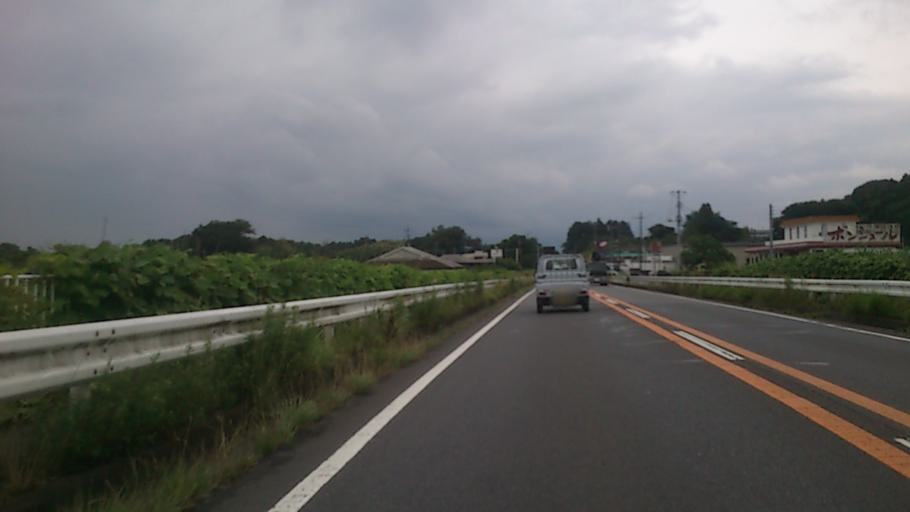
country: JP
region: Ibaraki
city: Ishioka
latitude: 36.1495
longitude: 140.2387
